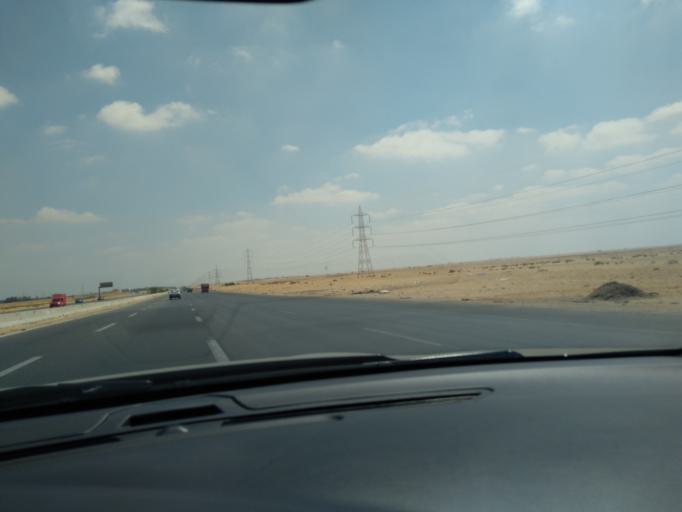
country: EG
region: Al Isma'iliyah
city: At Tall al Kabir
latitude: 30.3729
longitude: 31.9299
